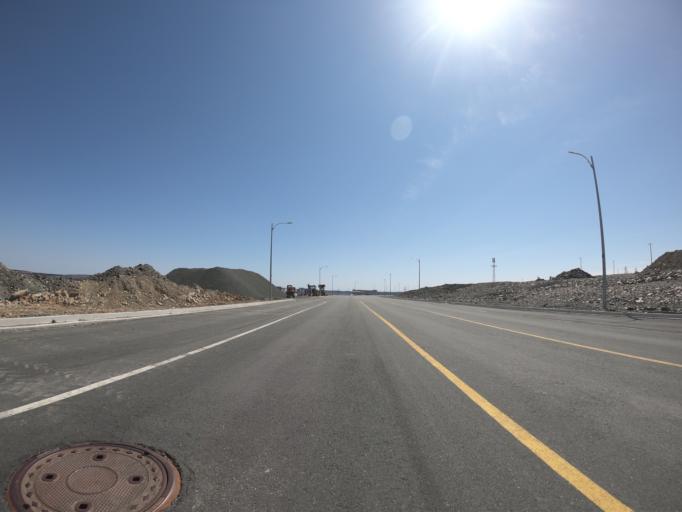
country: CA
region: Newfoundland and Labrador
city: Mount Pearl
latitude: 47.5090
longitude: -52.8347
